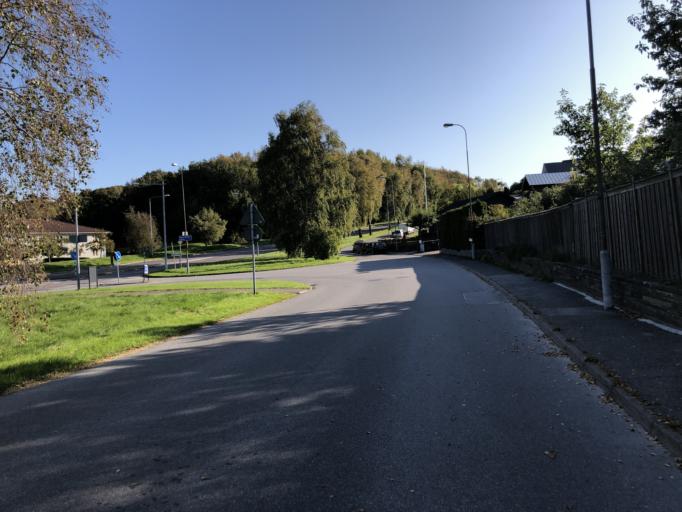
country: SE
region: Vaestra Goetaland
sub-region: Goteborg
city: Billdal
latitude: 57.6239
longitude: 11.9008
